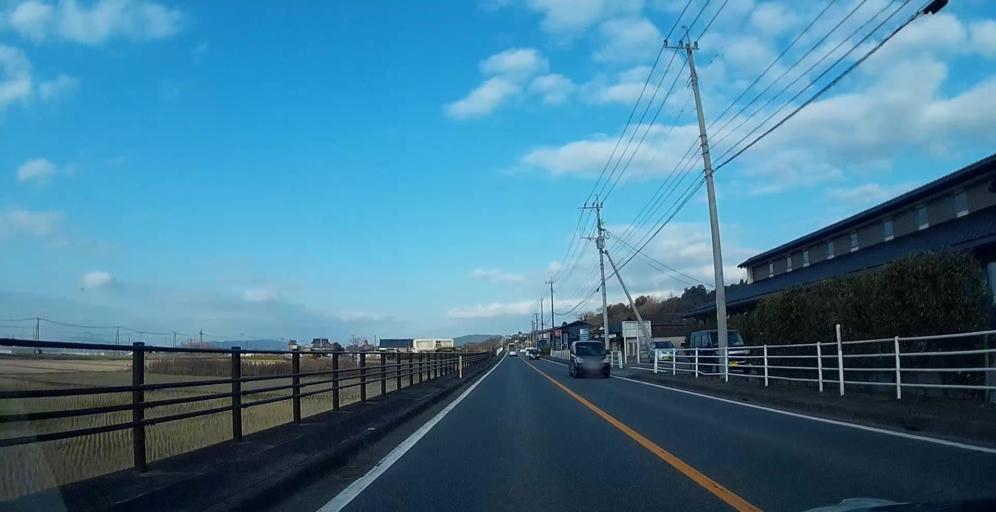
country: JP
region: Kumamoto
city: Matsubase
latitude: 32.5618
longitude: 130.6852
